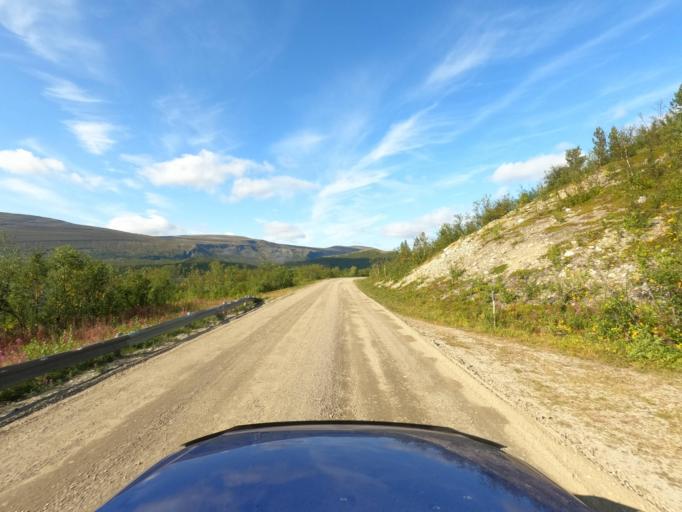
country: NO
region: Finnmark Fylke
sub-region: Porsanger
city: Lakselv
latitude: 69.8924
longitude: 24.9954
